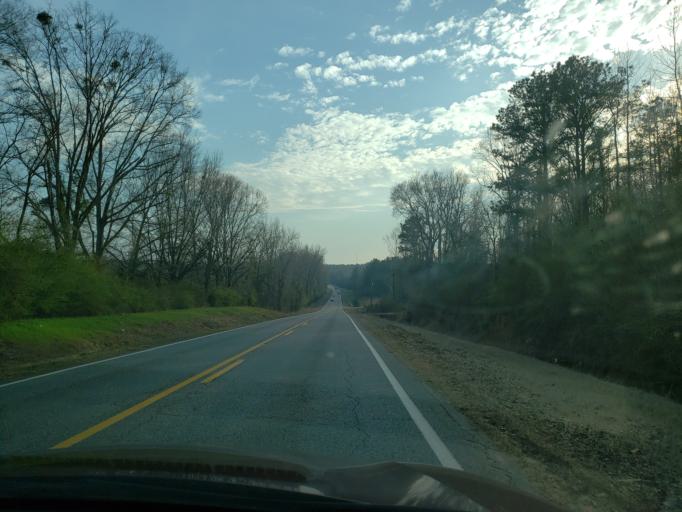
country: US
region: Alabama
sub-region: Hale County
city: Moundville
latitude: 32.9364
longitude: -87.6303
